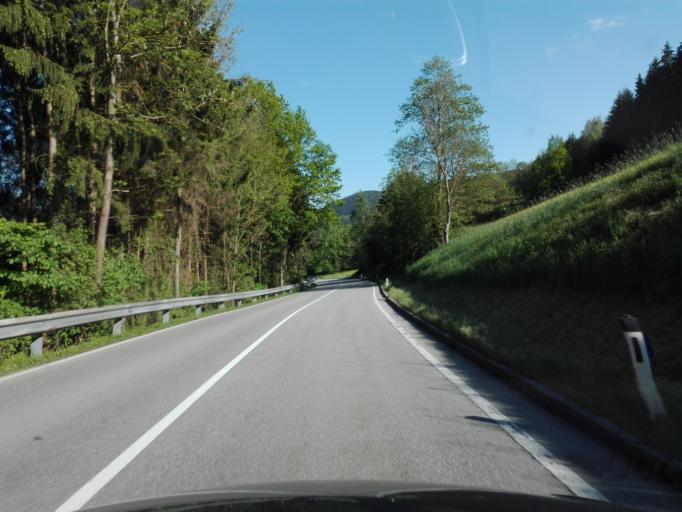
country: AT
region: Upper Austria
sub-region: Politischer Bezirk Rohrbach
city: Pfarrkirchen im Muehlkreis
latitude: 48.4770
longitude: 13.7662
